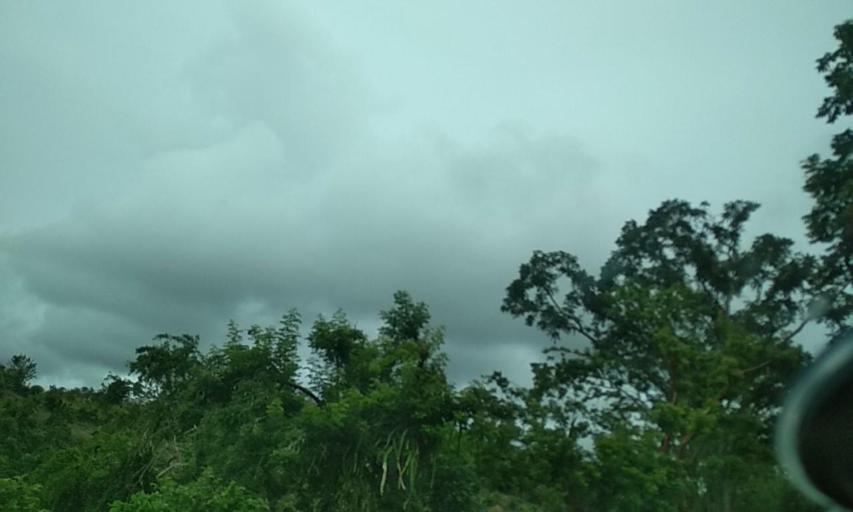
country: MX
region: Veracruz
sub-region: Papantla
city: Residencial Tajin
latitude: 20.6065
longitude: -97.3356
